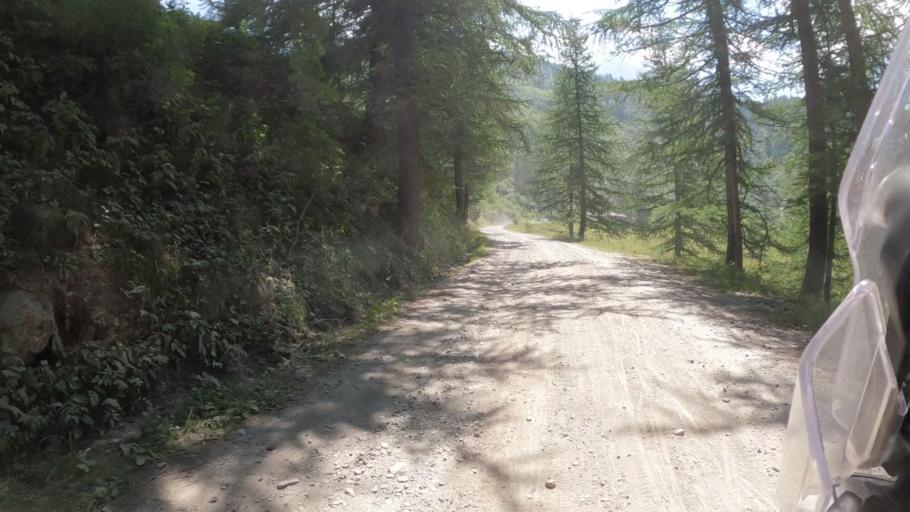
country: IT
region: Piedmont
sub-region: Provincia di Torino
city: Meana di Susa
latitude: 45.0892
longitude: 7.0622
